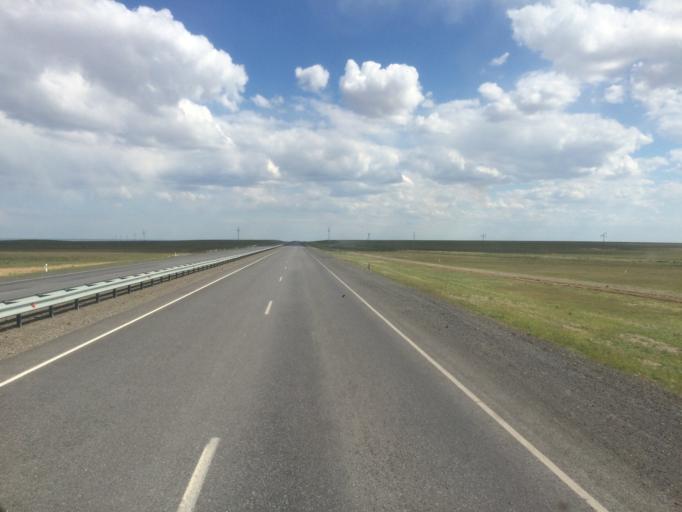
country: KZ
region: Qyzylorda
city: Shalqiya
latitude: 43.8617
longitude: 67.3976
